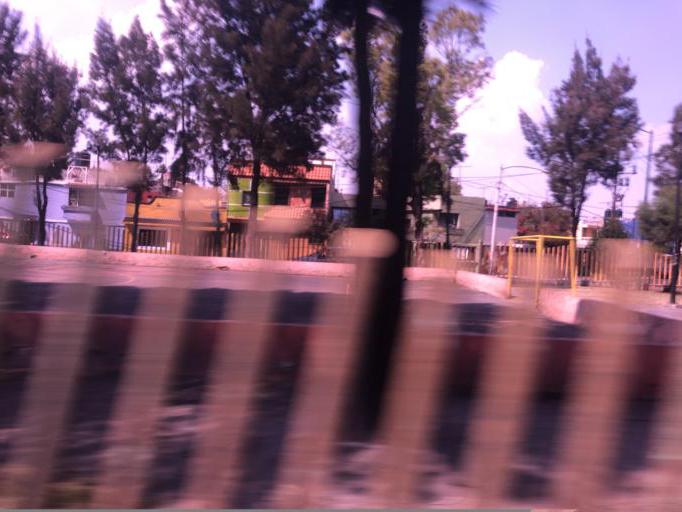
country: MX
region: Mexico City
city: Venustiano Carranza
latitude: 19.4520
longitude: -99.0530
